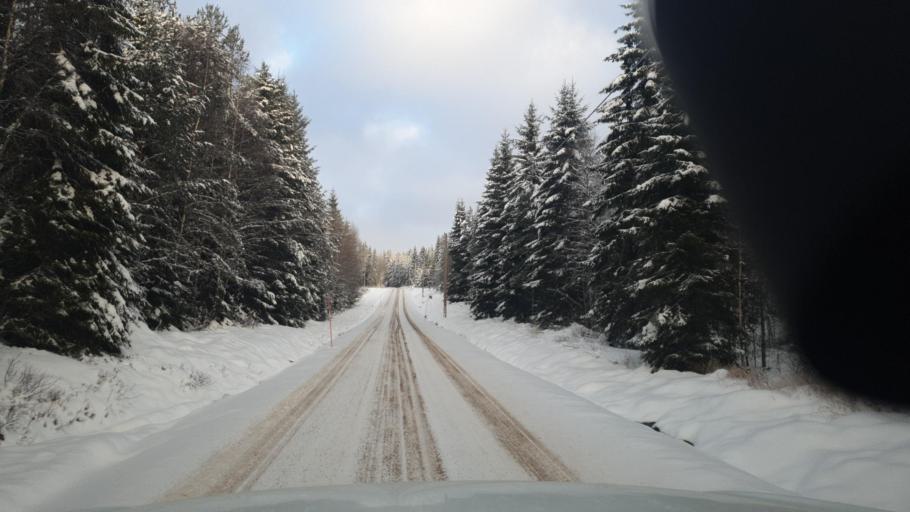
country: SE
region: Vaermland
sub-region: Eda Kommun
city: Charlottenberg
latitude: 60.1549
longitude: 12.5986
